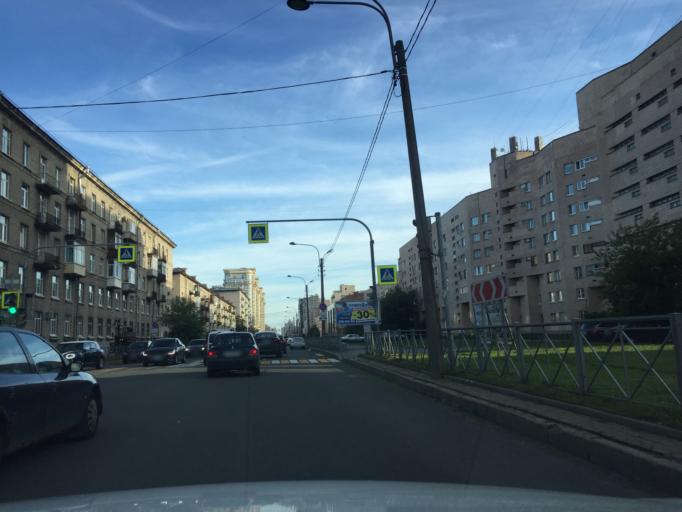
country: RU
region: St.-Petersburg
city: Kupchino
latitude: 59.8618
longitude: 30.3141
